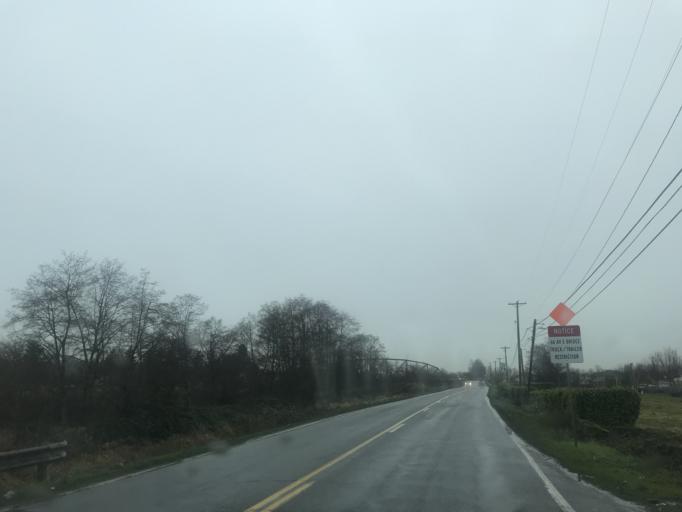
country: US
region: Washington
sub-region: Pierce County
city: Fife
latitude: 47.2124
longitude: -122.3372
